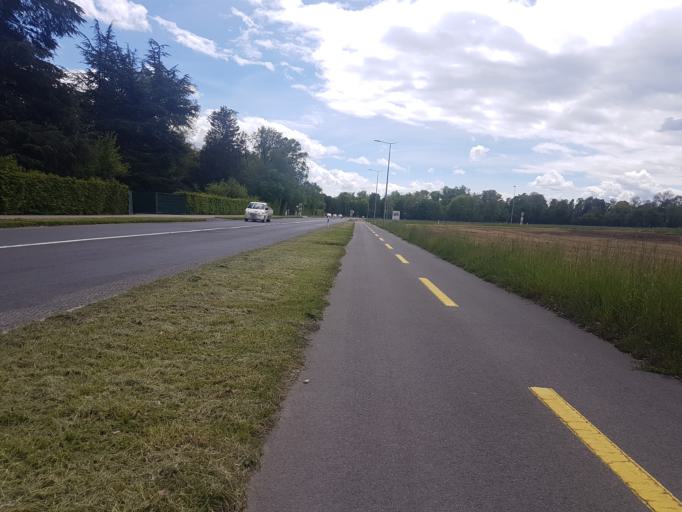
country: CH
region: Vaud
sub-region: Nyon District
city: Founex
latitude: 46.3438
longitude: 6.2057
